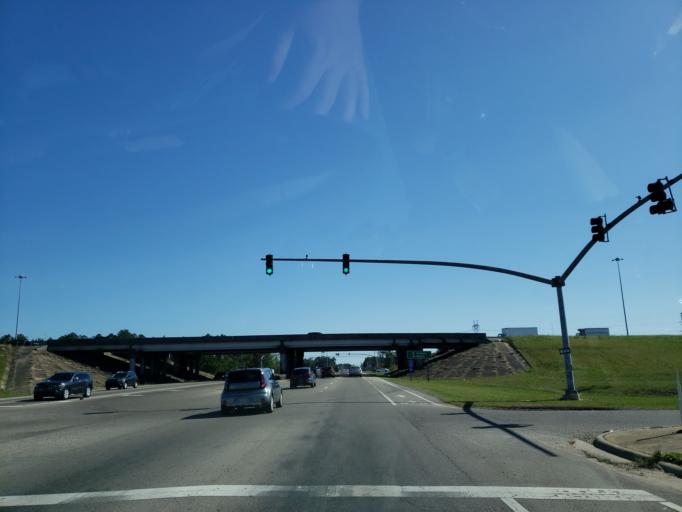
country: US
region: Mississippi
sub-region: Harrison County
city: West Gulfport
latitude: 30.4454
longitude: -89.0313
